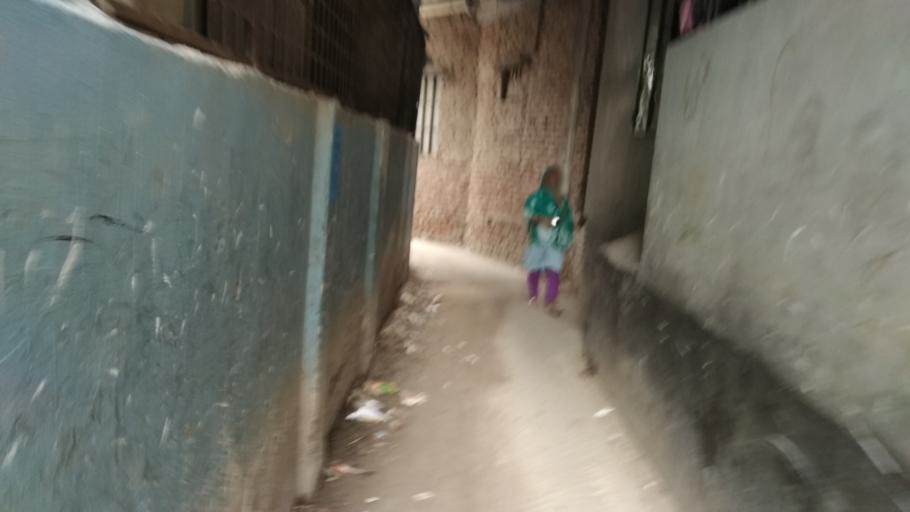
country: BD
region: Dhaka
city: Azimpur
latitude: 23.8024
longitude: 90.3734
